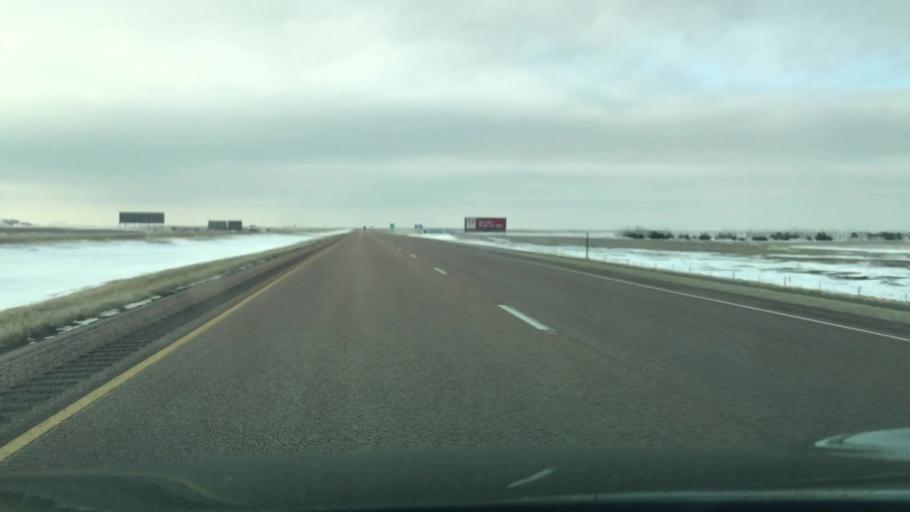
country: US
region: South Dakota
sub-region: Buffalo County
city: Fort Thompson
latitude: 43.8597
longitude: -99.5921
